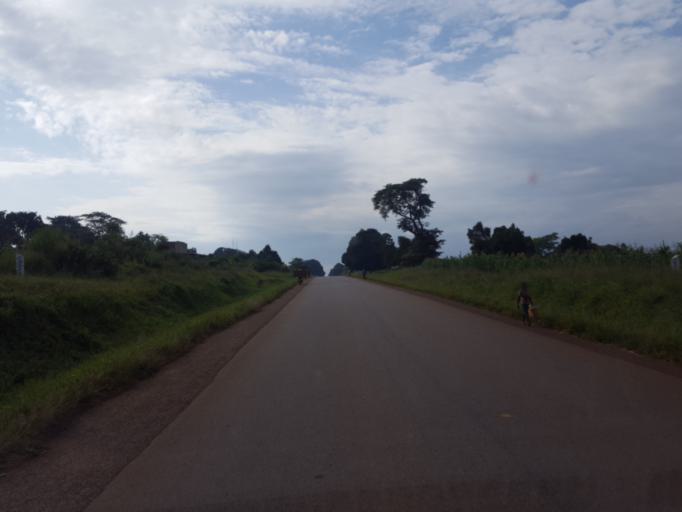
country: UG
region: Western Region
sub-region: Hoima District
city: Hoima
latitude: 1.2694
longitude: 31.4941
